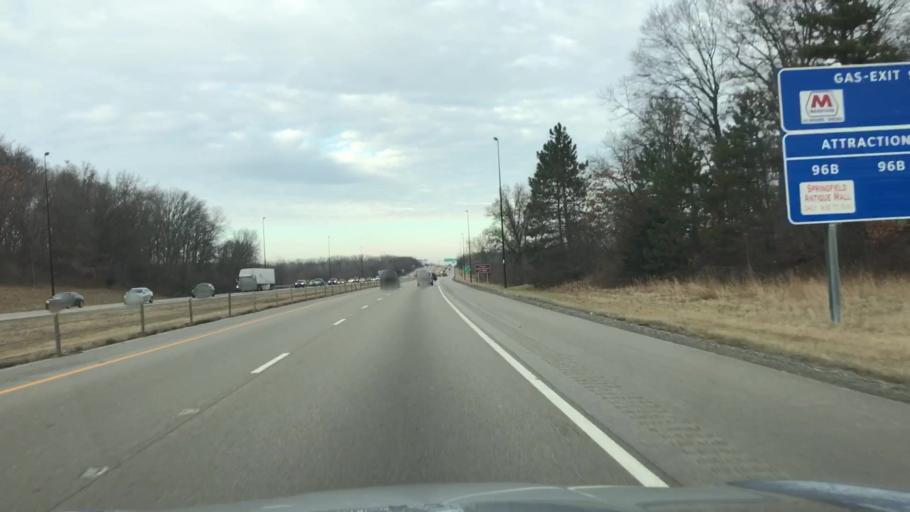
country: US
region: Illinois
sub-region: Sangamon County
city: Grandview
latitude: 39.7728
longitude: -89.6028
